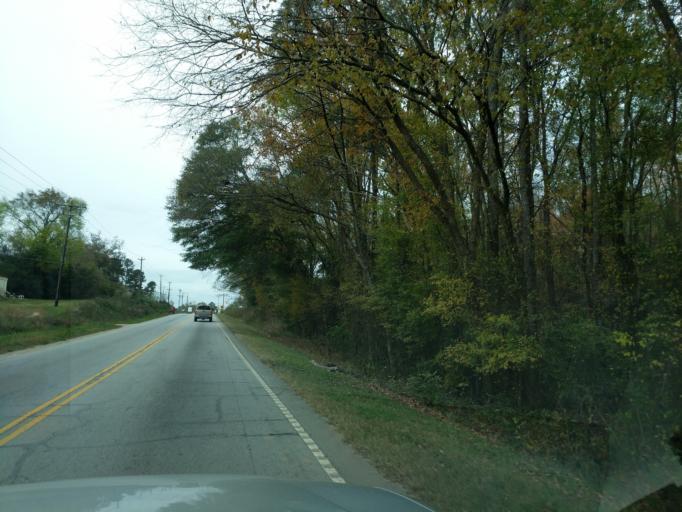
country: US
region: South Carolina
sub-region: Newberry County
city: Newberry
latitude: 34.2794
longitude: -81.6365
